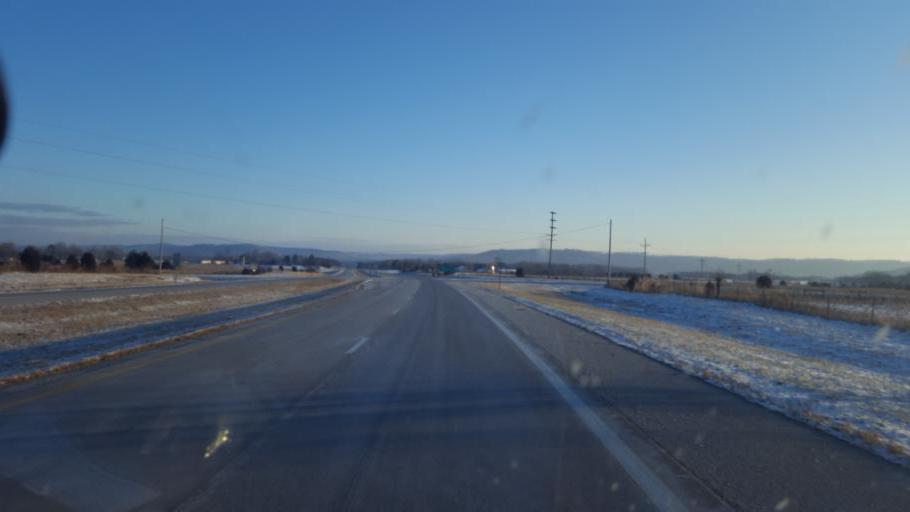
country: US
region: Ohio
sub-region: Adams County
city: Peebles
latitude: 38.9545
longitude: -83.3653
